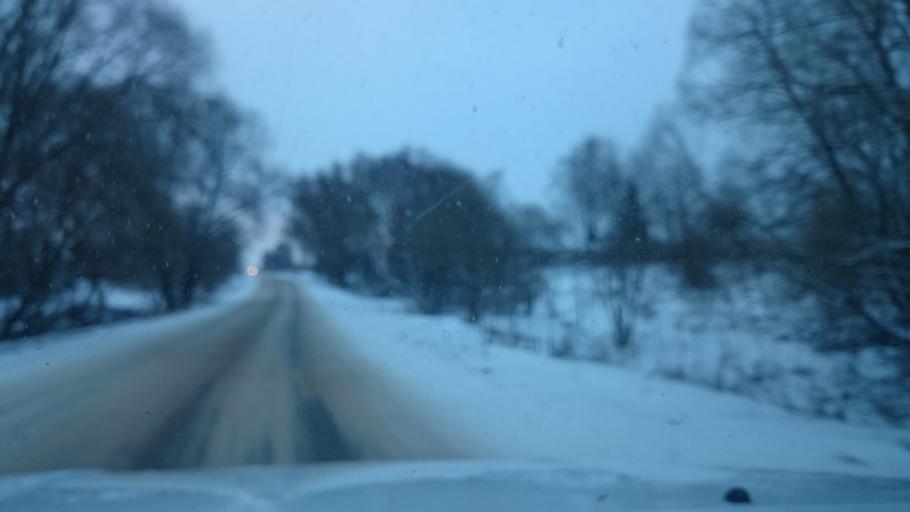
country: RU
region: Tula
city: Leninskiy
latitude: 54.2452
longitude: 37.2650
